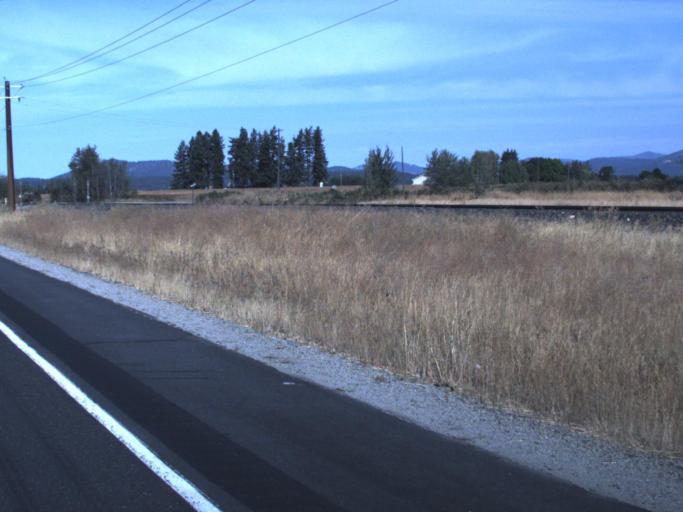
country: US
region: Washington
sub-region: Spokane County
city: Deer Park
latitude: 47.9707
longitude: -117.5120
